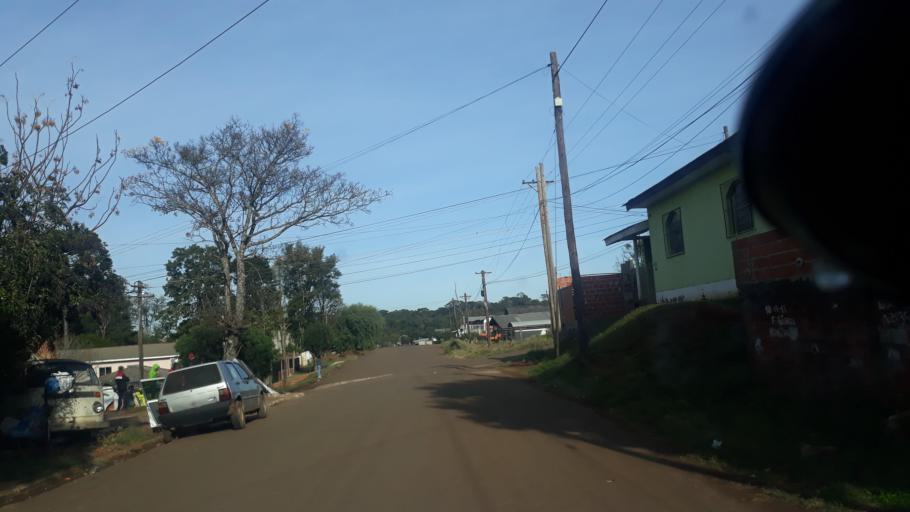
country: AR
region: Misiones
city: Bernardo de Irigoyen
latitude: -26.2647
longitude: -53.6507
